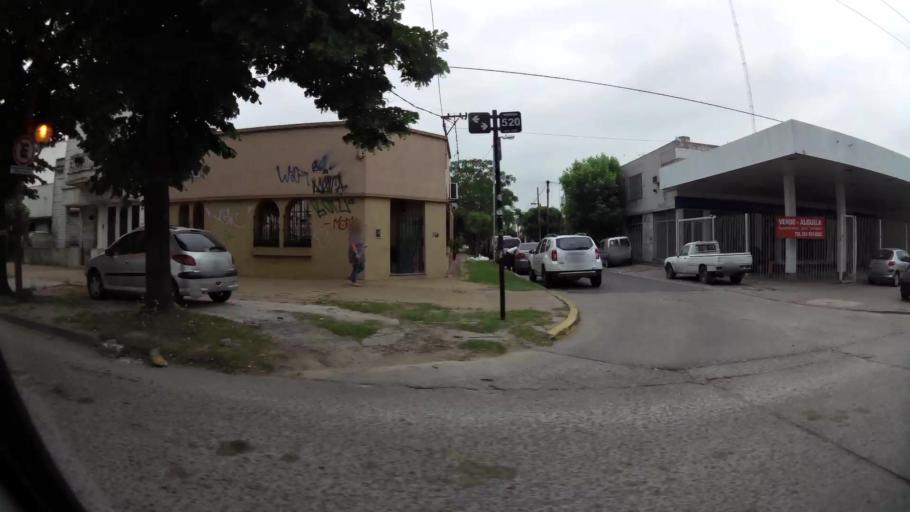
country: AR
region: Buenos Aires
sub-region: Partido de La Plata
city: La Plata
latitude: -34.8872
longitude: -57.9792
